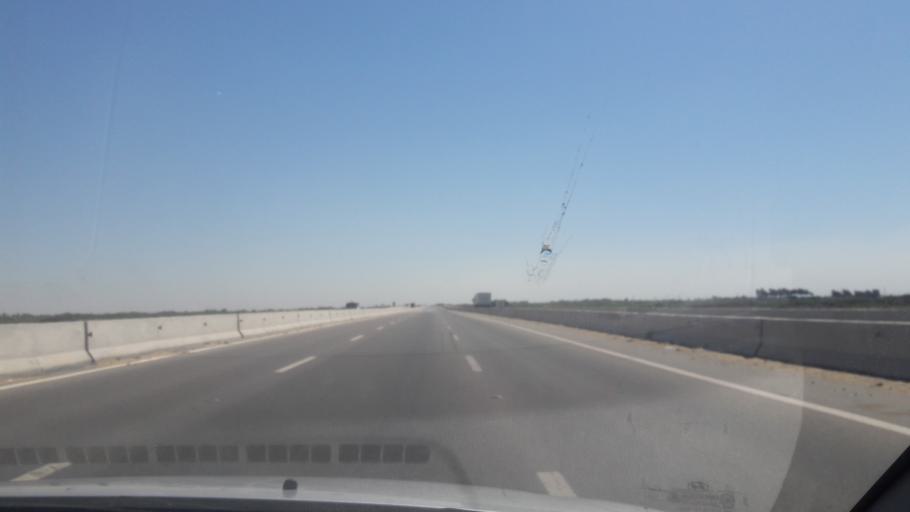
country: EG
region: Muhafazat ad Daqahliyah
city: Al Matariyah
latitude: 30.9112
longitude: 32.1877
